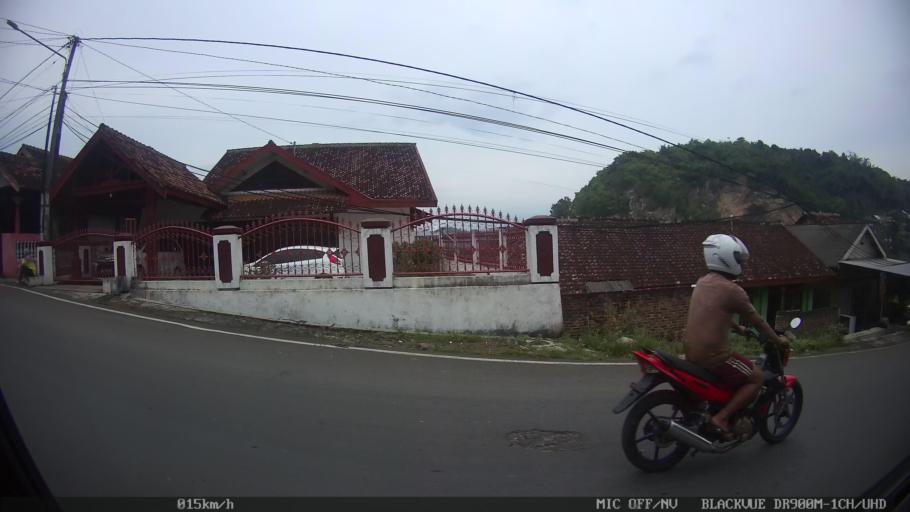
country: ID
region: Lampung
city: Bandarlampung
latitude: -5.4060
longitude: 105.2407
